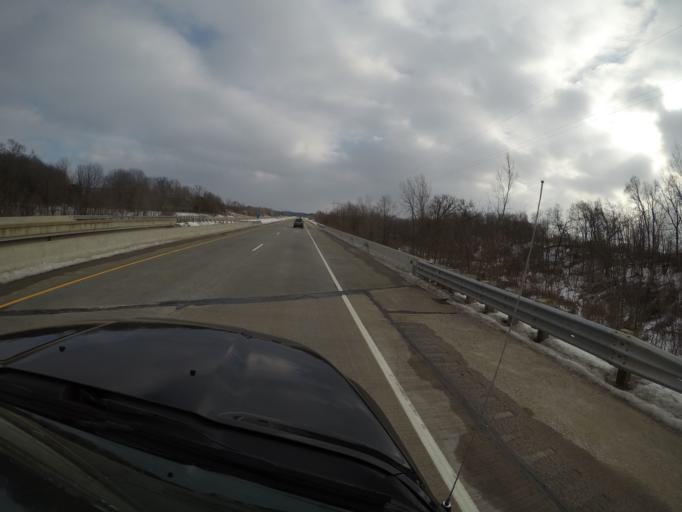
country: US
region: Wisconsin
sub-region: La Crosse County
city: Holmen
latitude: 43.9483
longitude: -91.2683
